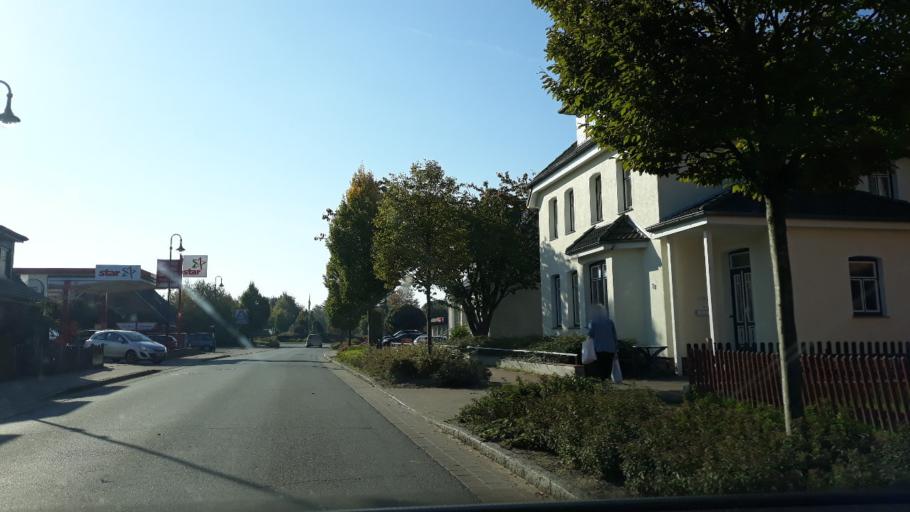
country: DE
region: Schleswig-Holstein
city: Boklund
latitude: 54.6022
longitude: 9.5840
